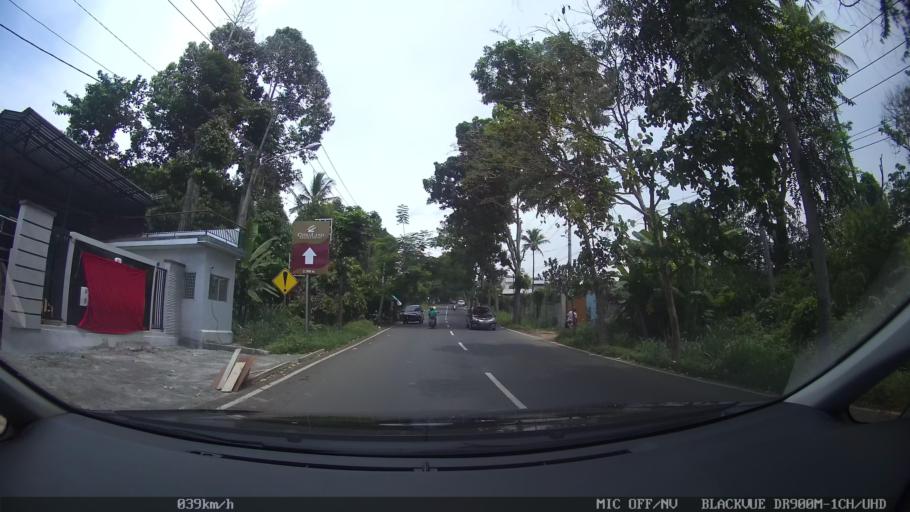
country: ID
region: Lampung
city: Bandarlampung
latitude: -5.4332
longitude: 105.2444
